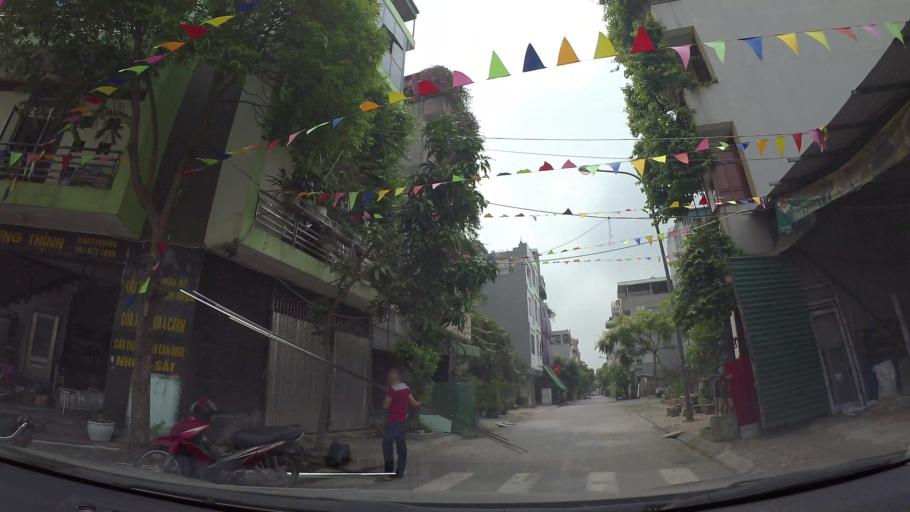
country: VN
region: Ha Noi
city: Trau Quy
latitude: 21.0658
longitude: 105.9162
